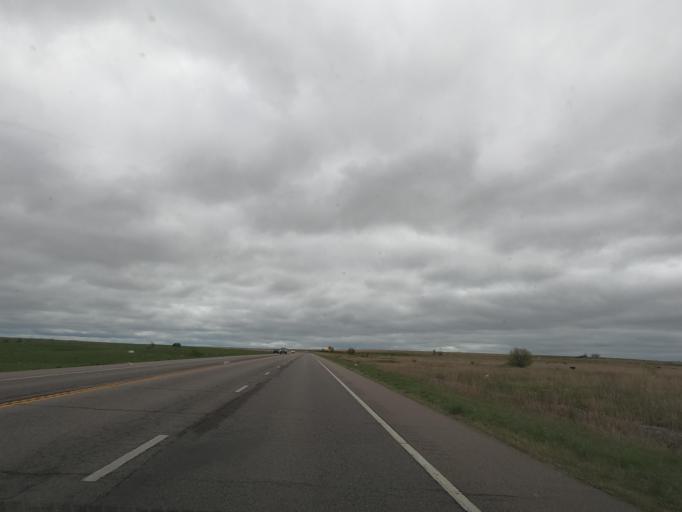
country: US
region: Kansas
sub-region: Greenwood County
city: Eureka
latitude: 37.6475
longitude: -96.4511
